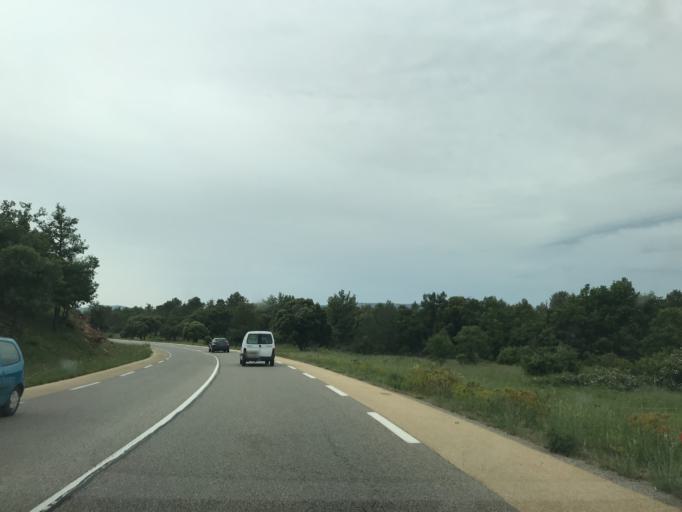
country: FR
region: Provence-Alpes-Cote d'Azur
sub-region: Departement du Var
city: Pourrieres
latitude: 43.5123
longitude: 5.8011
